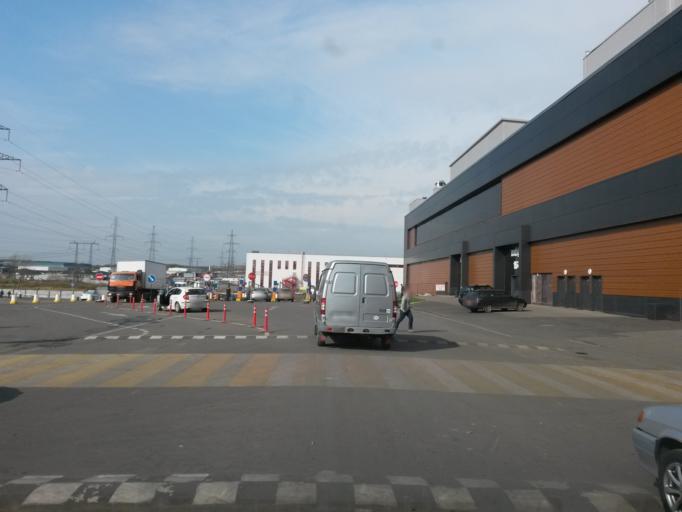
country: RU
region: Moskovskaya
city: Mosrentgen
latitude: 55.6011
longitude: 37.4674
